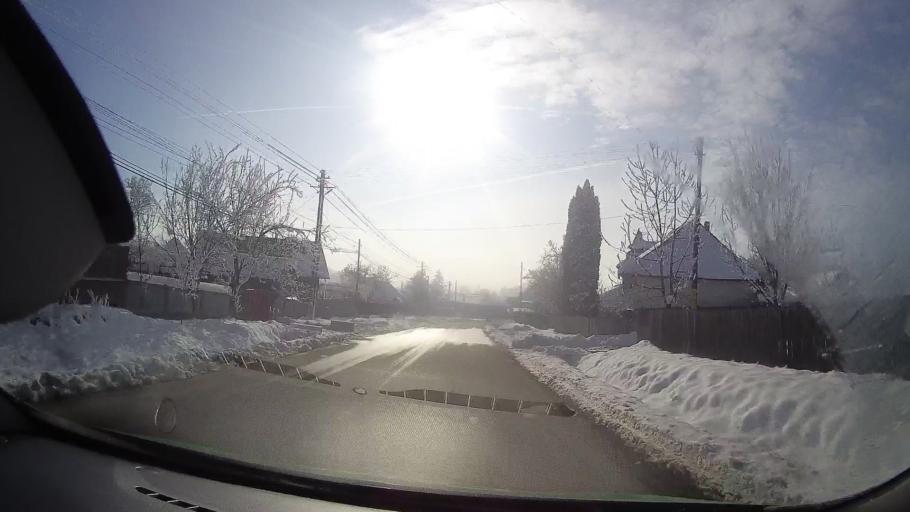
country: RO
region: Iasi
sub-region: Comuna Cristesti
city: Cristesti
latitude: 47.2566
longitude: 26.5749
